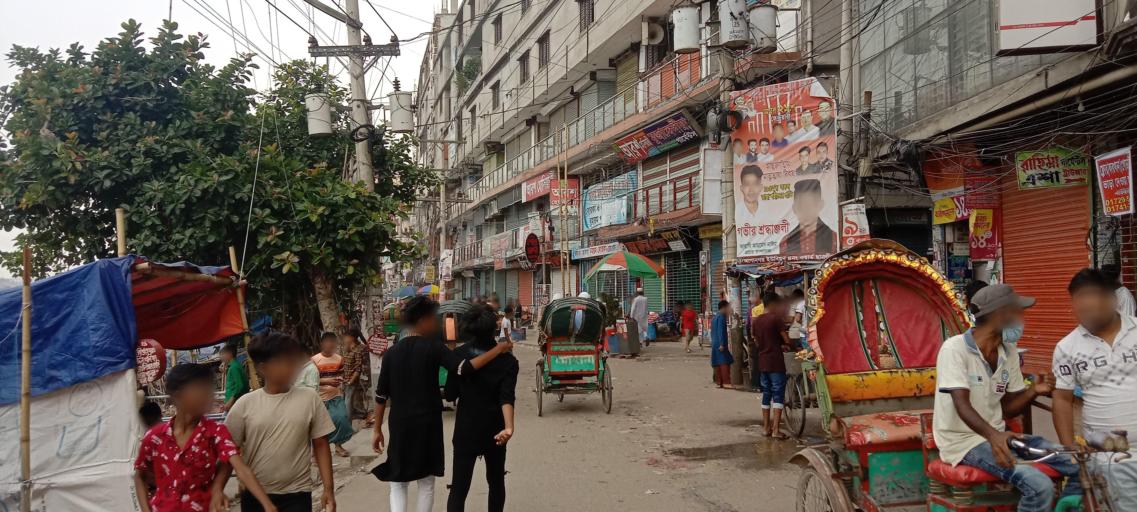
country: BD
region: Dhaka
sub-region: Dhaka
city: Dhaka
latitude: 23.7051
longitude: 90.4049
